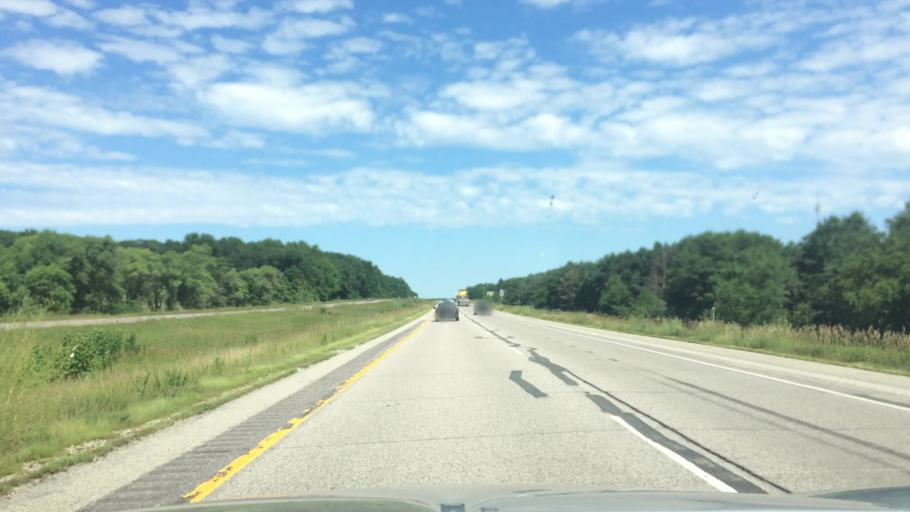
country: US
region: Wisconsin
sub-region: Marquette County
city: Westfield
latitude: 43.7195
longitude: -89.4777
